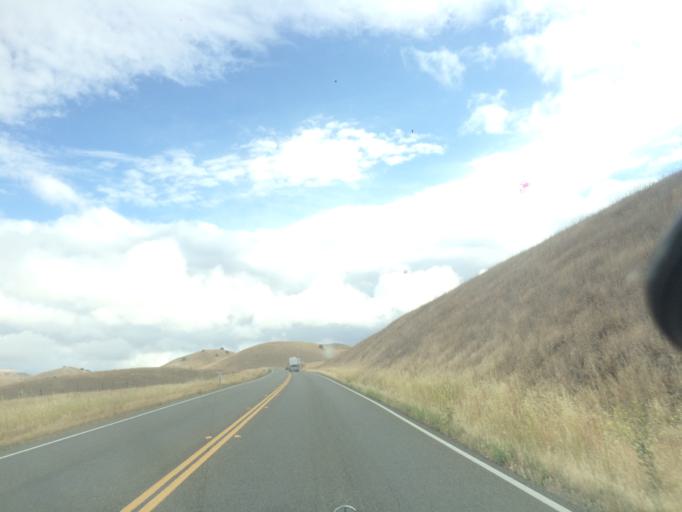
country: US
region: California
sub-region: San Luis Obispo County
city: Shandon
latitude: 35.7626
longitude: -120.2538
